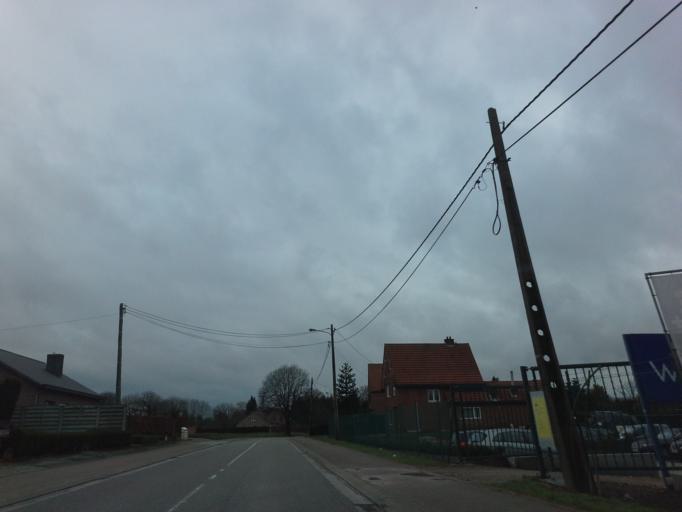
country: BE
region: Flanders
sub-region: Provincie Antwerpen
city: Meerhout
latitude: 51.1388
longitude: 5.0882
